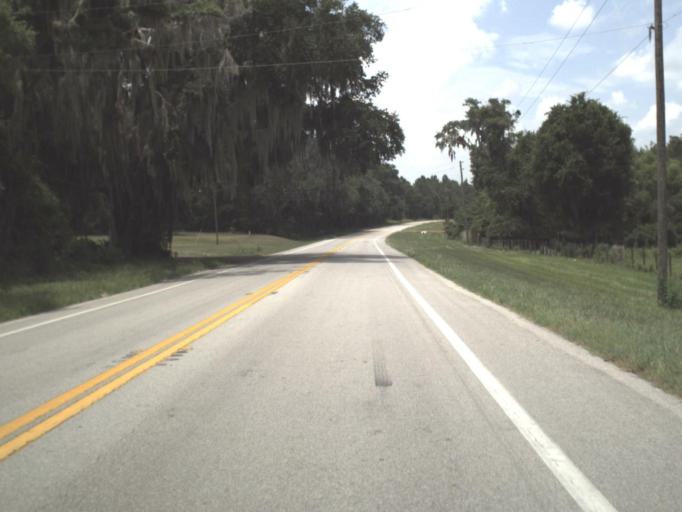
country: US
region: Florida
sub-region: Madison County
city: Madison
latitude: 30.5004
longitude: -83.4230
